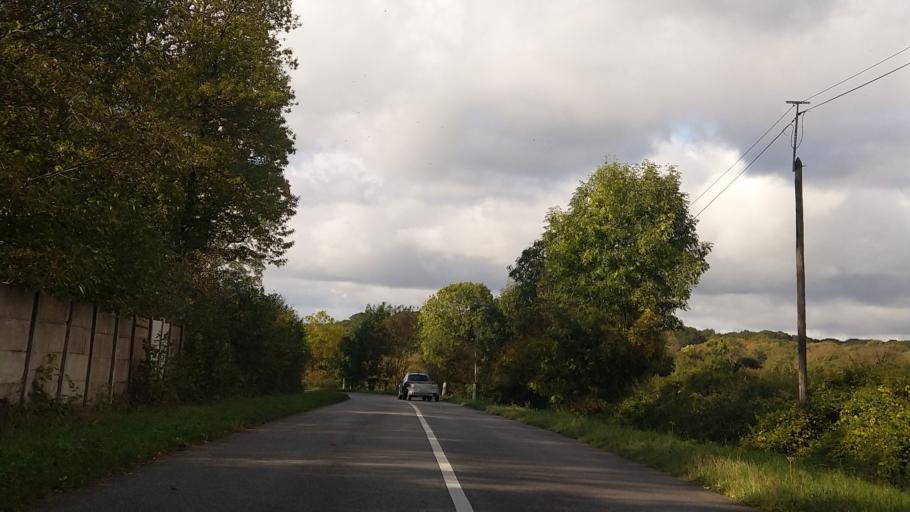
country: FR
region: Ile-de-France
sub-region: Departement du Val-d'Oise
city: Baillet-en-France
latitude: 49.0681
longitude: 2.2894
